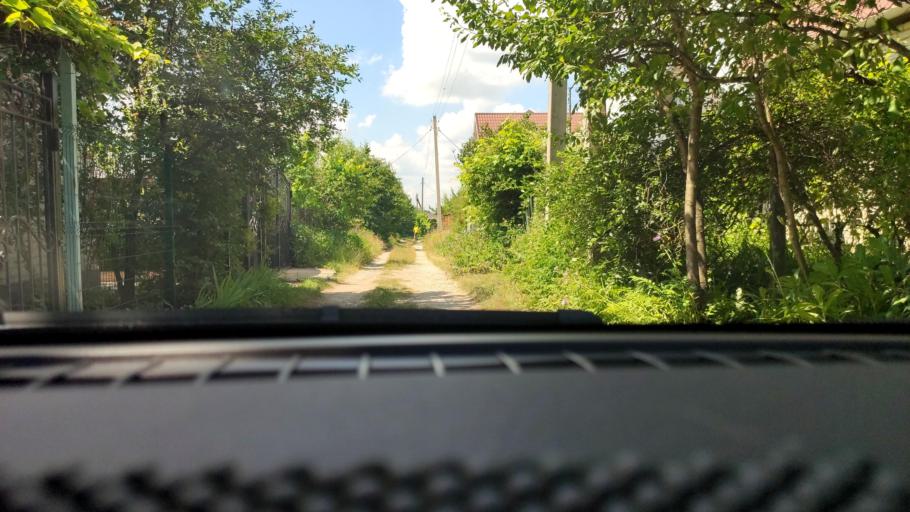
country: RU
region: Voronezj
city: Ramon'
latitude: 51.9113
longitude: 39.1774
